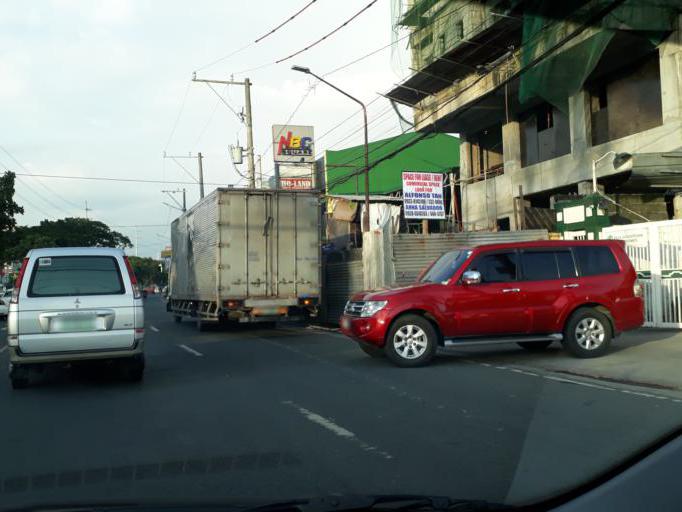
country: PH
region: Calabarzon
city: Bagong Pagasa
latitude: 14.6683
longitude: 121.0344
